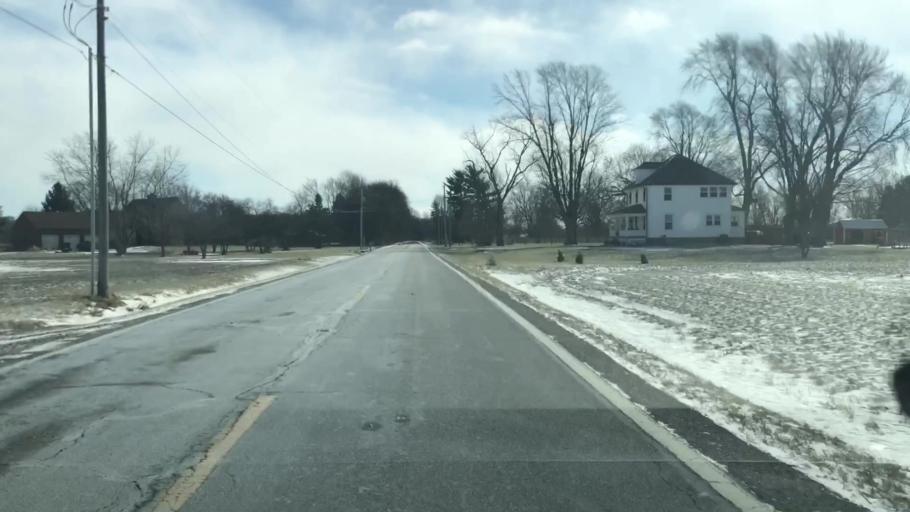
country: US
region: Ohio
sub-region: Franklin County
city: Hilliard
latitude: 40.0235
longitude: -83.2224
